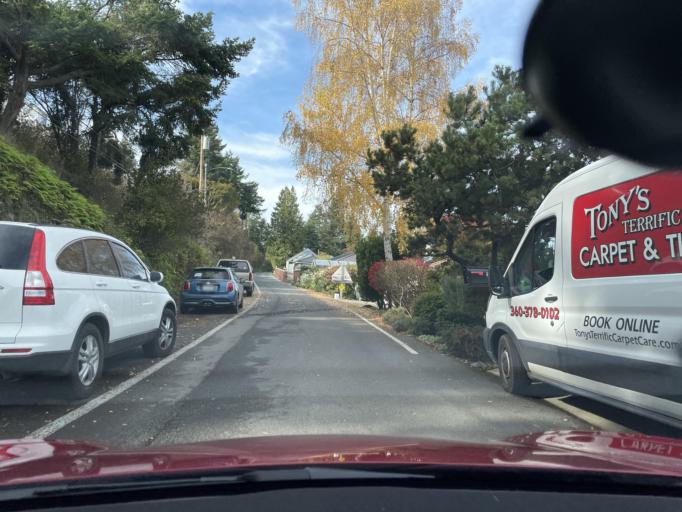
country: US
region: Washington
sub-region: San Juan County
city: Friday Harbor
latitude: 48.5336
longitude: -123.0085
